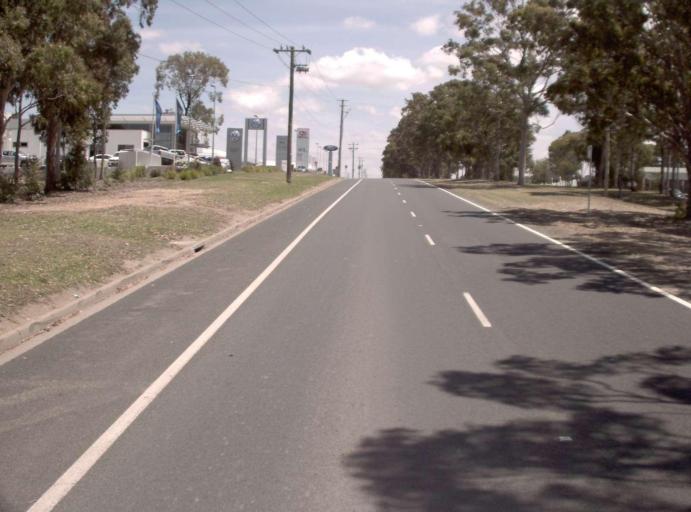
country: AU
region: Victoria
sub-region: East Gippsland
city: Bairnsdale
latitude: -37.8317
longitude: 147.6100
